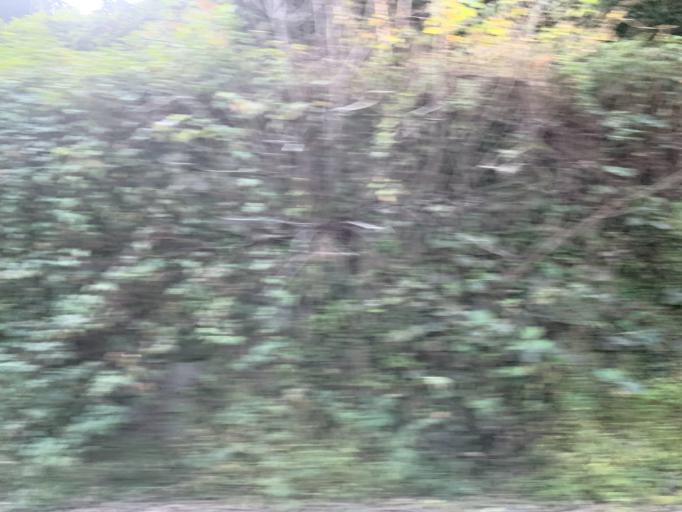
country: TR
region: Trabzon
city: Dernekpazari
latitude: 40.8655
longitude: 40.2787
